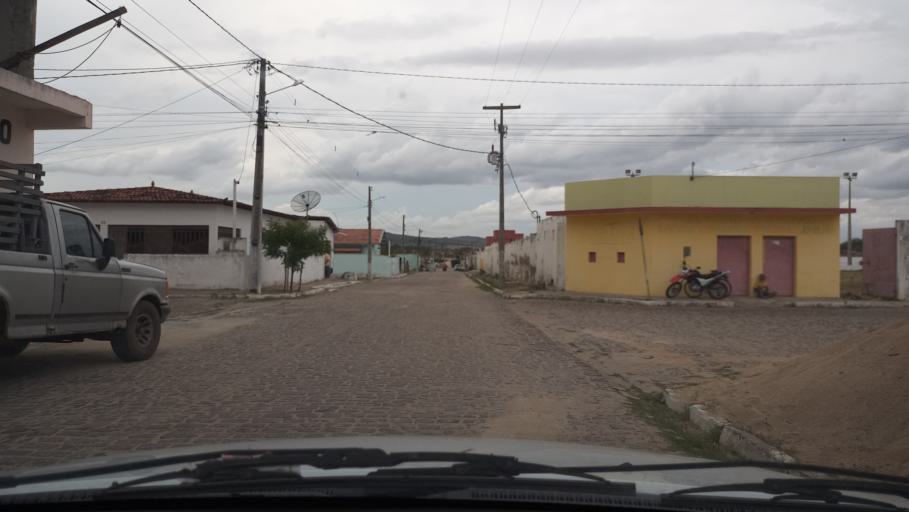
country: BR
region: Rio Grande do Norte
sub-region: Tangara
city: Tangara
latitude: -6.1978
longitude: -35.8004
